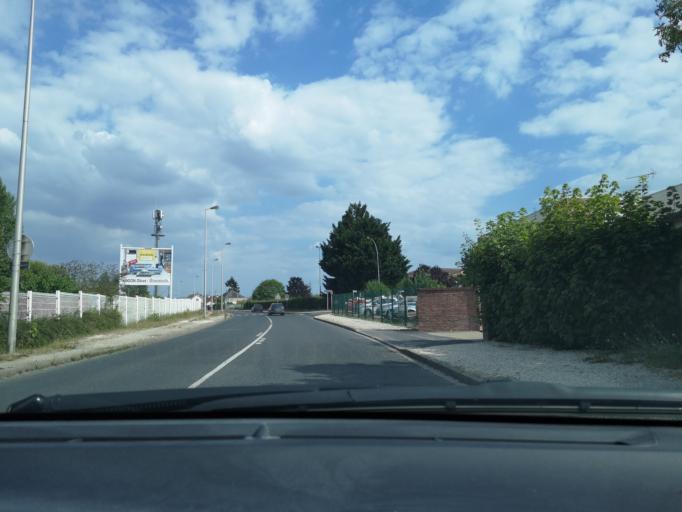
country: FR
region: Centre
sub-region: Departement du Loiret
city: Semoy
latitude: 47.9397
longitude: 1.9352
